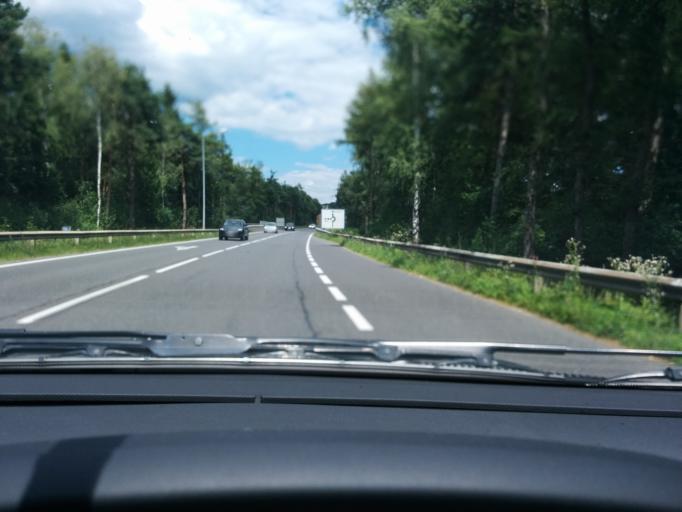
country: AT
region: Styria
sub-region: Politischer Bezirk Weiz
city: Gleisdorf
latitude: 47.1094
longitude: 15.7004
